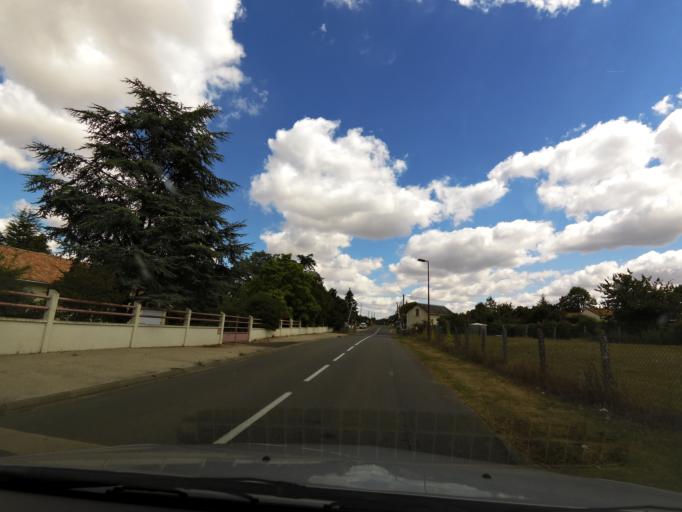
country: FR
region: Poitou-Charentes
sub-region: Departement des Deux-Sevres
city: Beauvoir-sur-Niort
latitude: 46.1779
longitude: -0.4670
